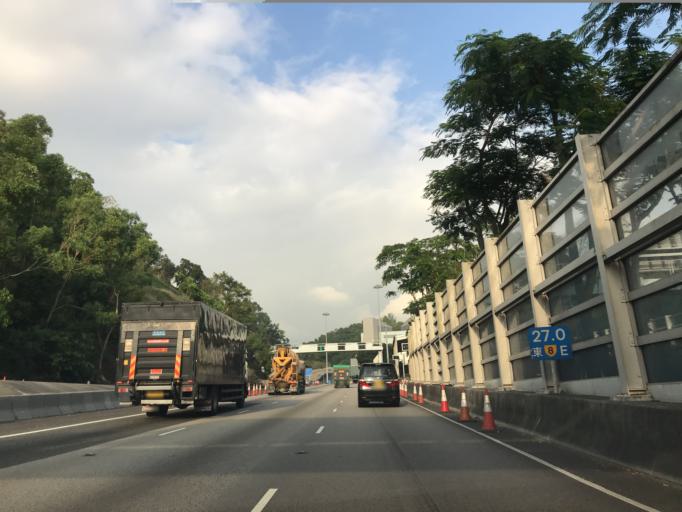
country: HK
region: Sham Shui Po
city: Sham Shui Po
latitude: 22.3444
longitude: 114.1450
